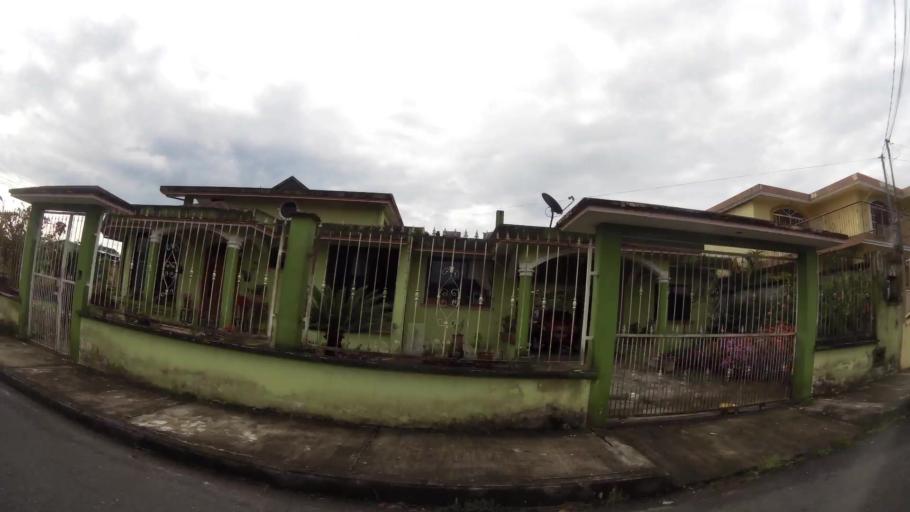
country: EC
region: Pastaza
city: Puyo
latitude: -1.4754
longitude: -78.0013
